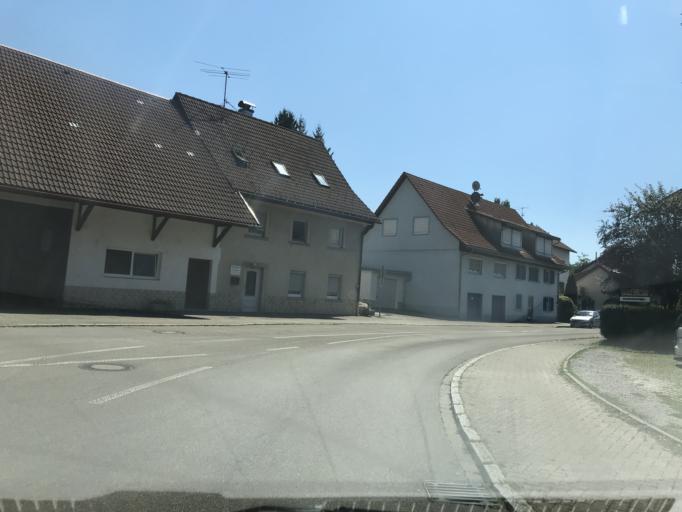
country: DE
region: Baden-Wuerttemberg
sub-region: Freiburg Region
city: Wehr
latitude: 47.6332
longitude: 7.9004
